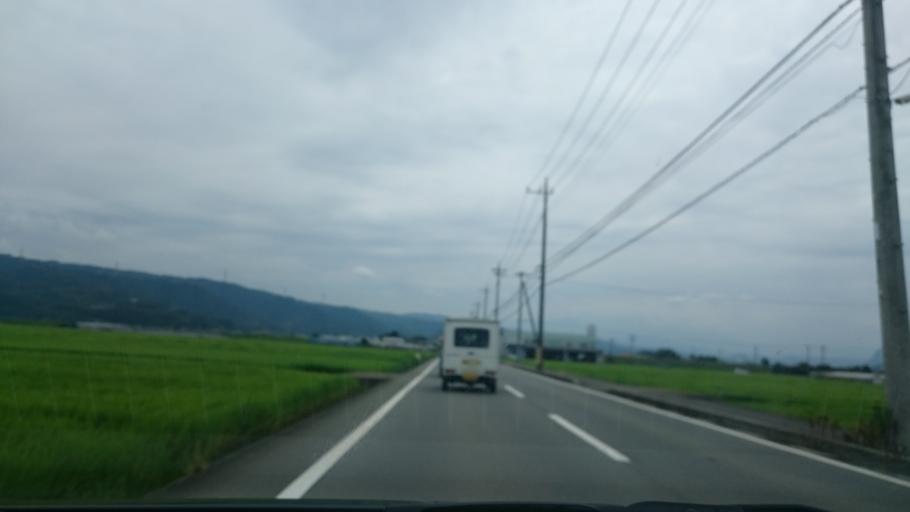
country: JP
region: Shizuoka
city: Mishima
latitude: 35.0765
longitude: 138.9478
